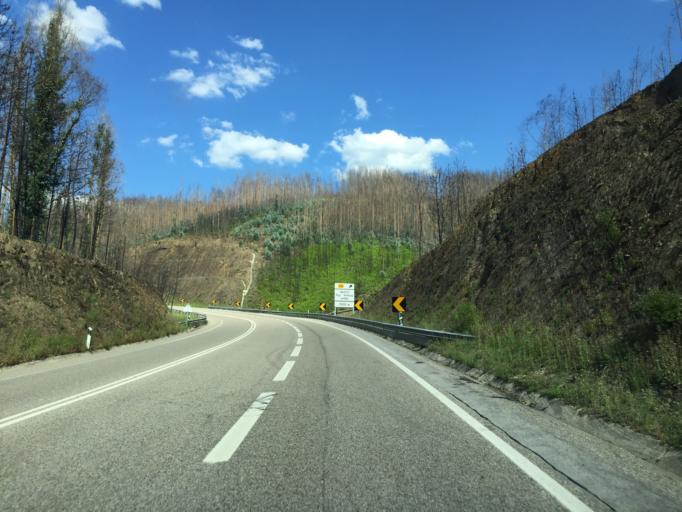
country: PT
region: Leiria
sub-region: Figueiro Dos Vinhos
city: Figueiro dos Vinhos
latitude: 39.9267
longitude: -8.3038
